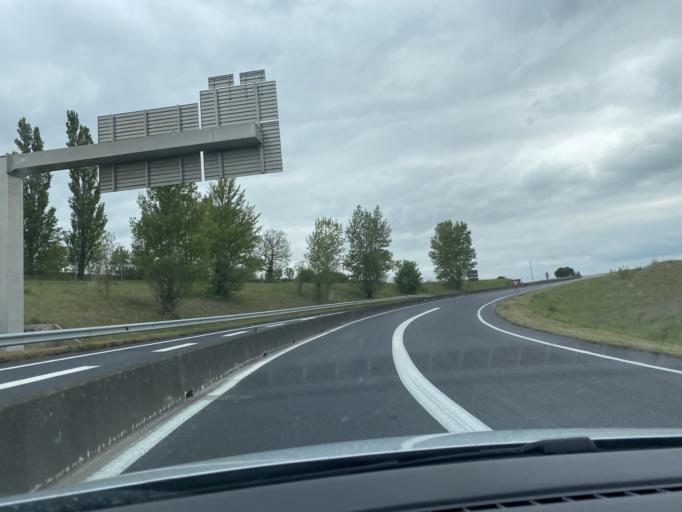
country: FR
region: Midi-Pyrenees
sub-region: Departement de la Haute-Garonne
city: Nailloux
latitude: 43.3838
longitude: 1.6219
